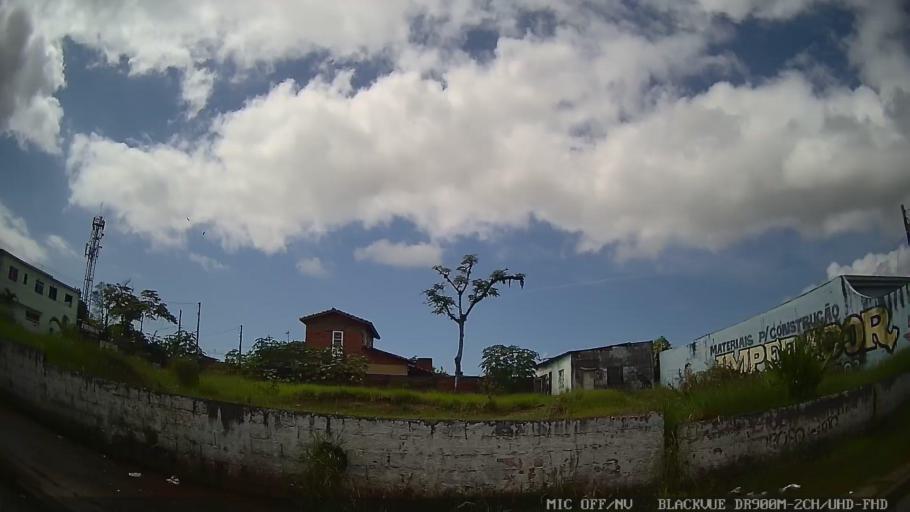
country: BR
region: Sao Paulo
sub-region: Peruibe
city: Peruibe
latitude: -24.2974
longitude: -47.0232
